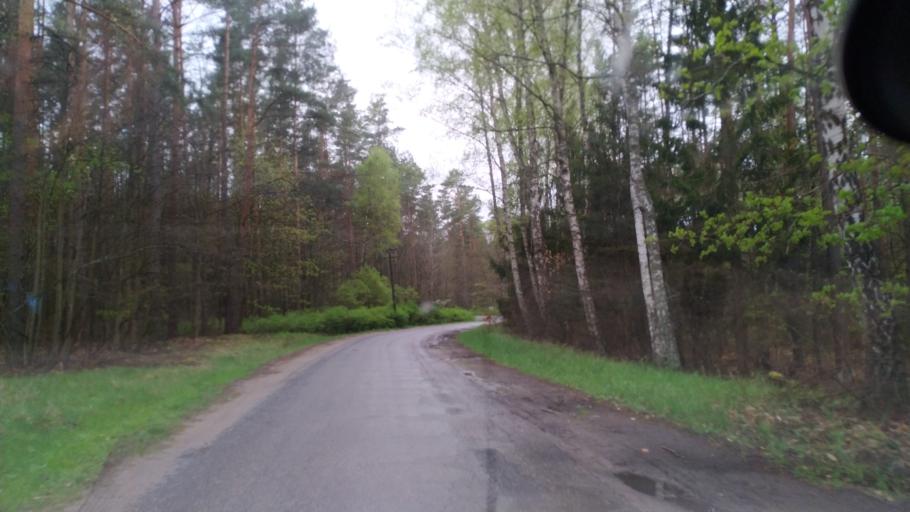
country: PL
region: Pomeranian Voivodeship
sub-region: Powiat starogardzki
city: Osiek
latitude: 53.6752
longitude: 18.4770
